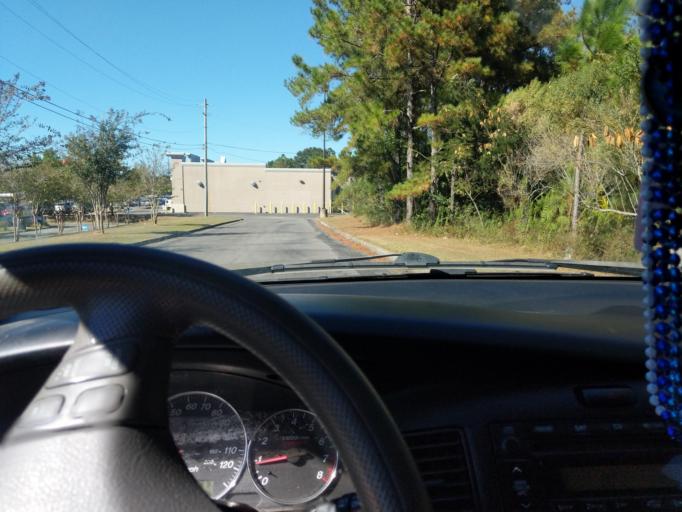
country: US
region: Alabama
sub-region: Houston County
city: Dothan
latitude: 31.1773
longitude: -85.4005
